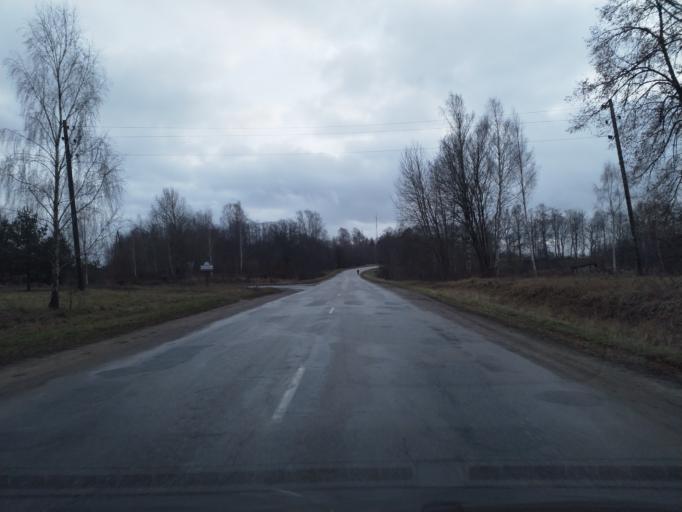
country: LV
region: Kuldigas Rajons
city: Kuldiga
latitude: 56.9502
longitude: 21.9966
